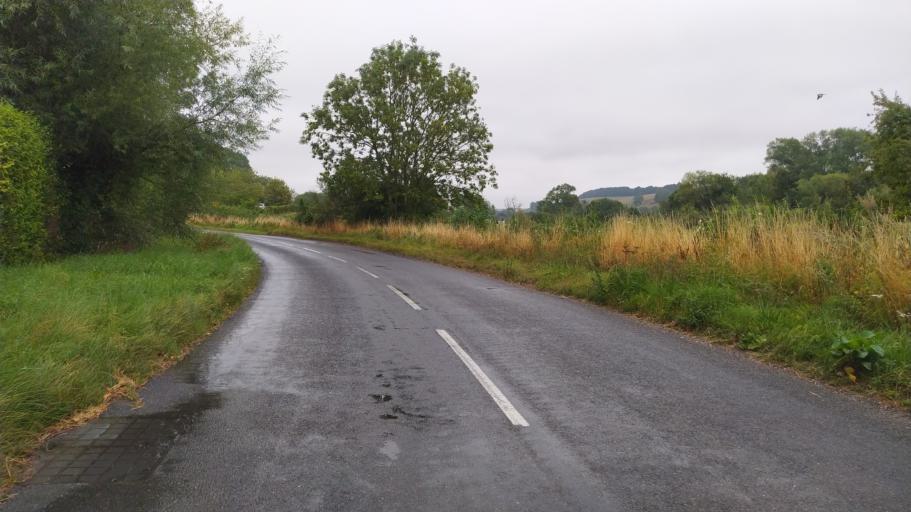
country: GB
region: England
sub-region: Wiltshire
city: Bower Chalke
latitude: 51.0292
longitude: -1.9444
